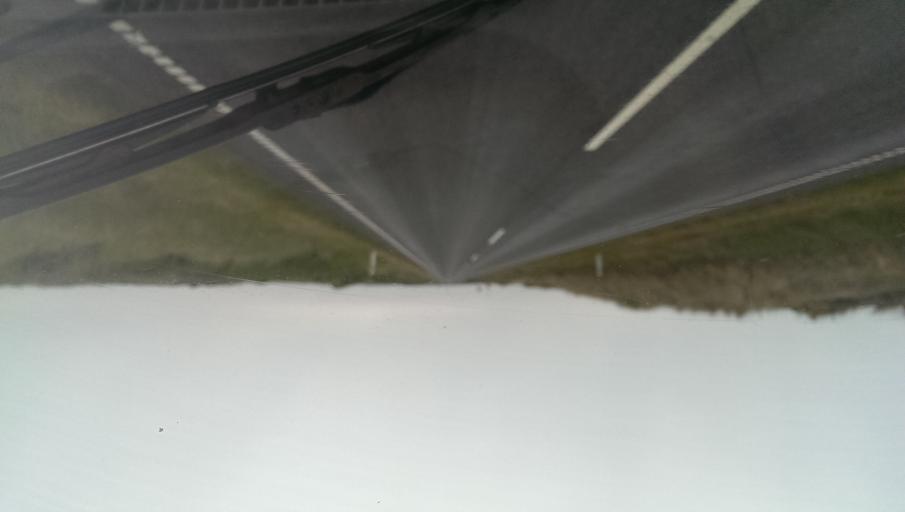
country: DK
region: Central Jutland
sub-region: Ringkobing-Skjern Kommune
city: Hvide Sande
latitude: 55.8295
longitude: 8.1727
